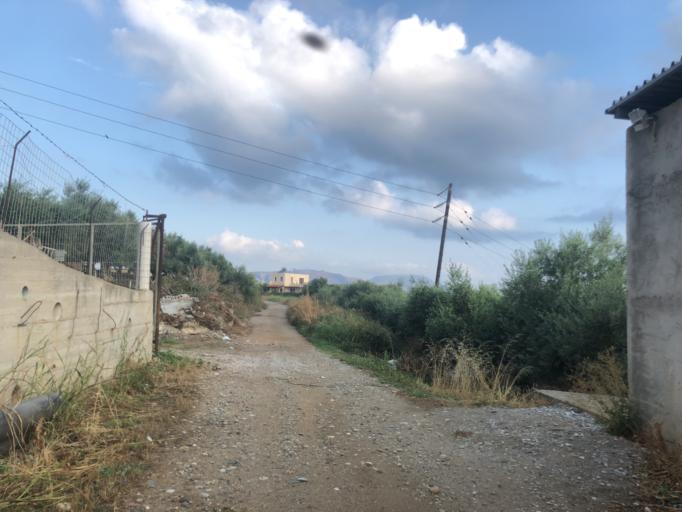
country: GR
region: Crete
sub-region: Nomos Chanias
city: Georgioupolis
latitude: 35.3469
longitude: 24.3116
